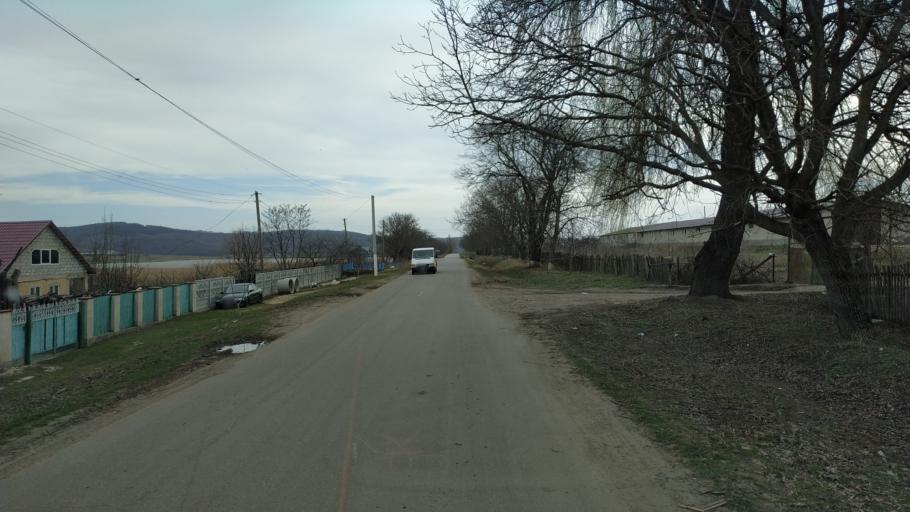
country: MD
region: Hincesti
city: Dancu
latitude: 46.9086
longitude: 28.2692
